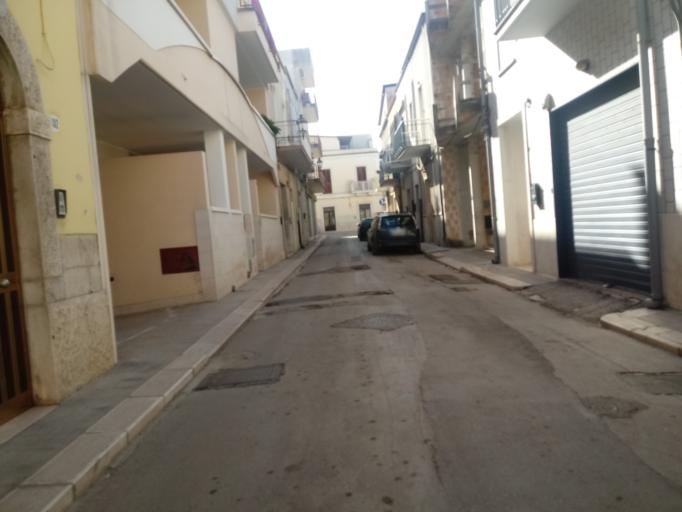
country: IT
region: Apulia
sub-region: Provincia di Barletta - Andria - Trani
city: Andria
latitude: 41.2218
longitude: 16.2961
